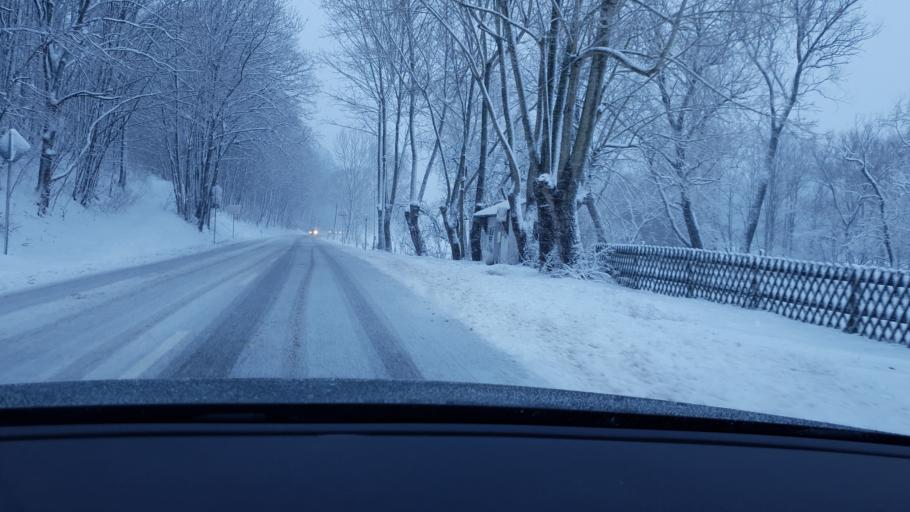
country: DE
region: Saxony
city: Claussnitz
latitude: 50.9149
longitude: 12.8997
